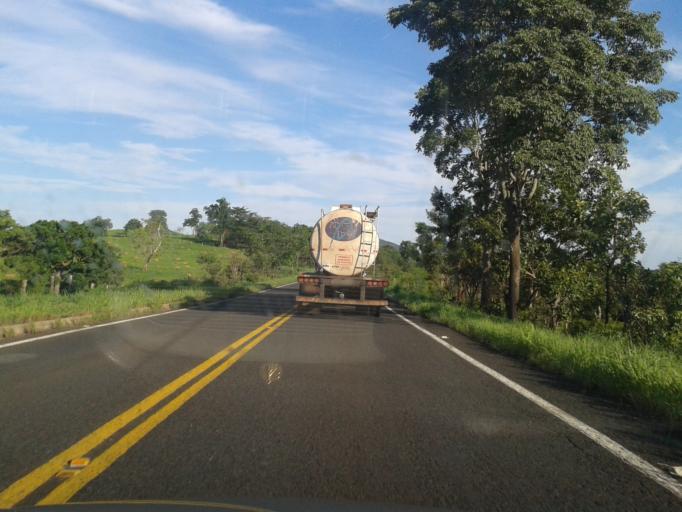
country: BR
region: Minas Gerais
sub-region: Tupaciguara
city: Tupaciguara
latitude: -18.2209
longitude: -48.5730
